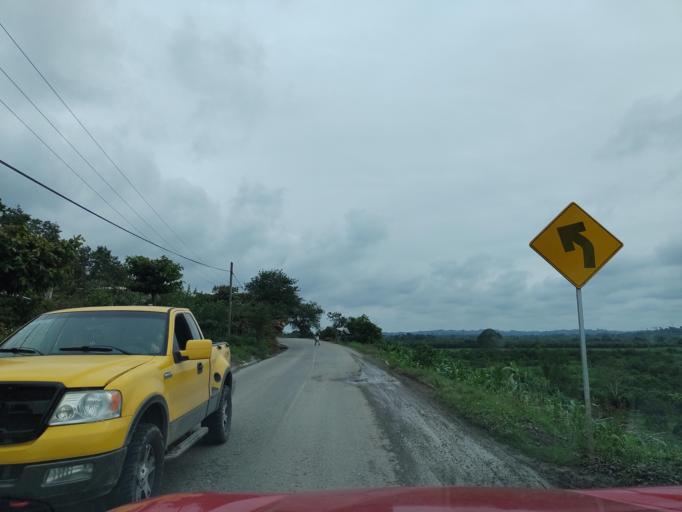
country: MX
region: Puebla
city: Espinal
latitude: 20.2618
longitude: -97.3668
